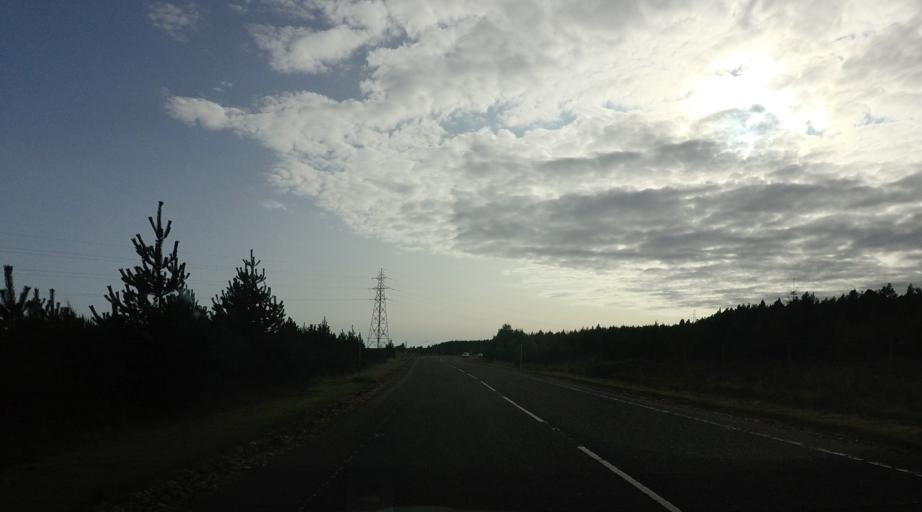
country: GB
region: Scotland
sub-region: Highland
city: Brora
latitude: 58.1472
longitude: -3.5980
